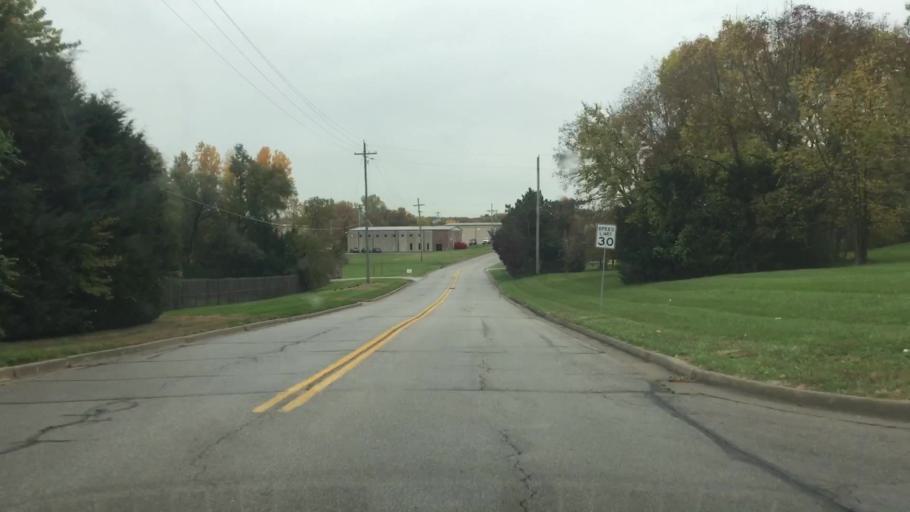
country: US
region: Kansas
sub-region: Wyandotte County
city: Edwardsville
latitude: 39.0072
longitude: -94.8236
